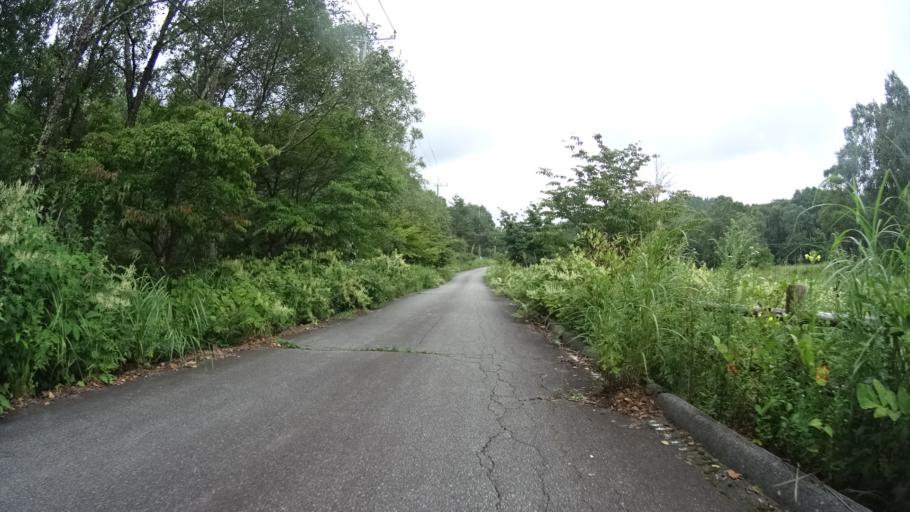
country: JP
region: Yamanashi
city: Enzan
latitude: 35.8007
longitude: 138.6342
